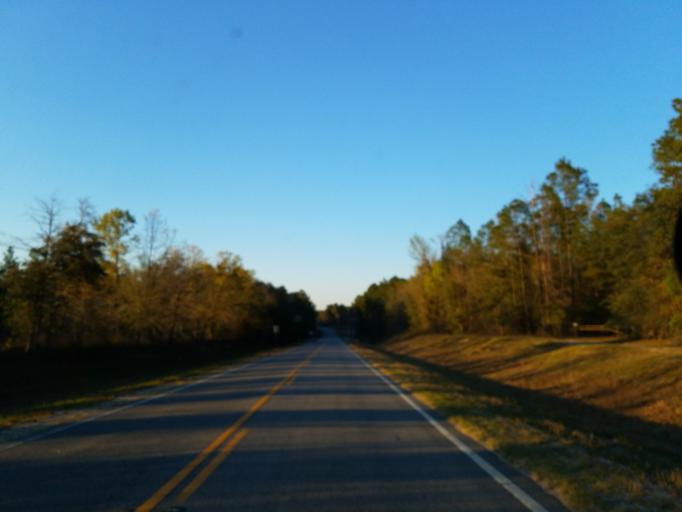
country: US
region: Georgia
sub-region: Echols County
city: Statenville
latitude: 30.8583
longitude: -83.0015
